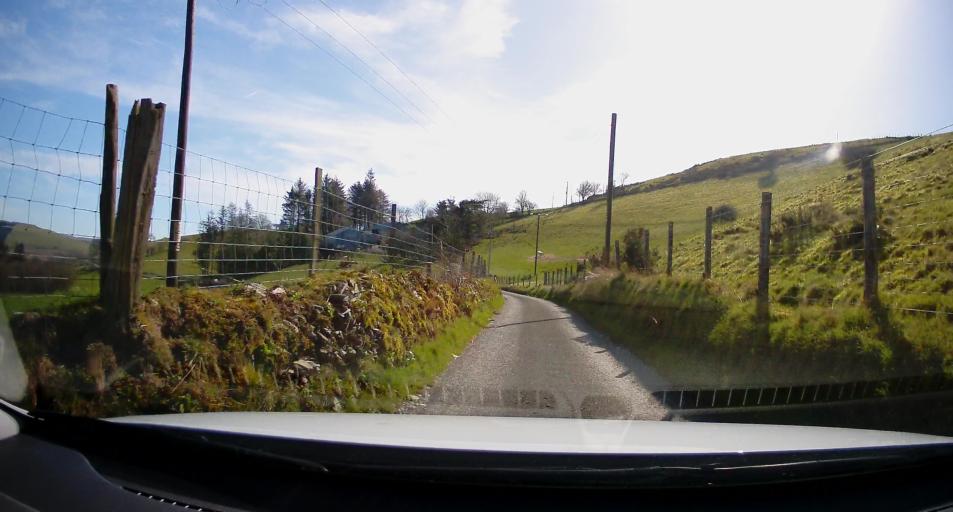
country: GB
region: Wales
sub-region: County of Ceredigion
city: Lledrod
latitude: 52.3700
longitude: -3.8671
